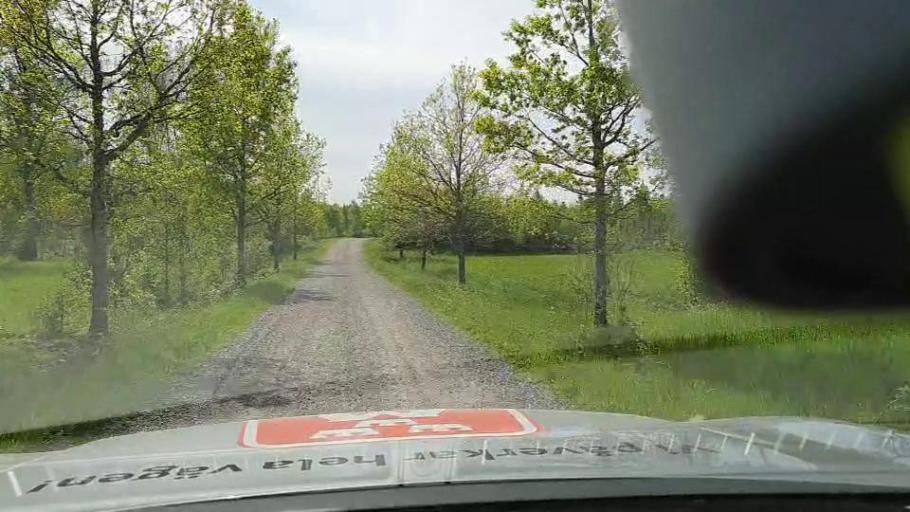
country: SE
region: Soedermanland
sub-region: Eskilstuna Kommun
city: Skogstorp
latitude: 59.2497
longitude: 16.5007
